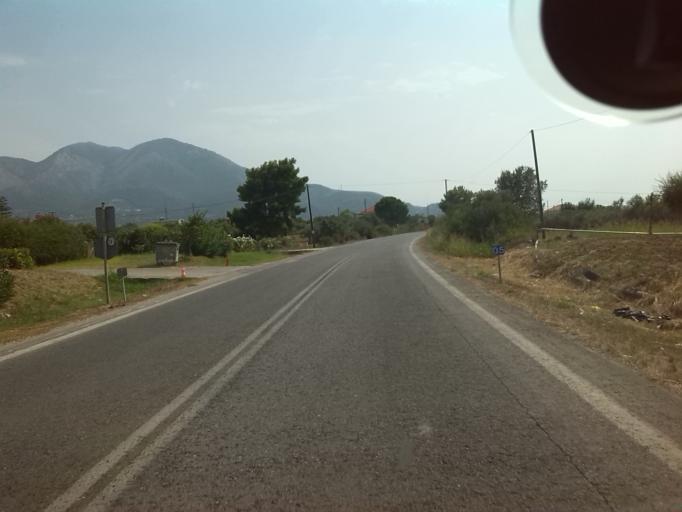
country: GR
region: Peloponnese
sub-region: Nomos Messinias
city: Kyparissia
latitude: 37.2831
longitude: 21.7011
